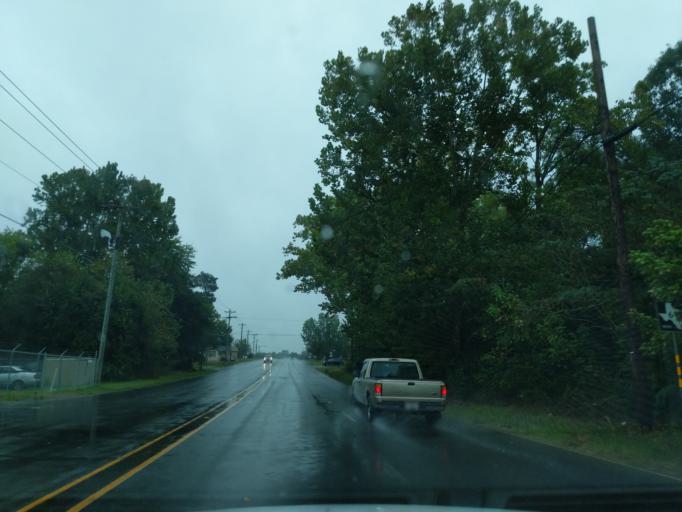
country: US
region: Texas
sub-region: Panola County
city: Carthage
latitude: 32.1578
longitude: -94.3306
